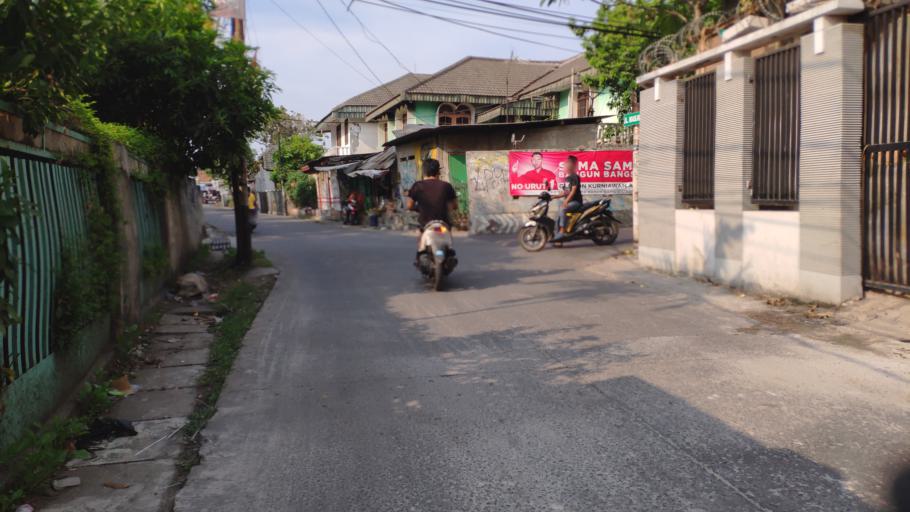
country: ID
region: West Java
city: Pamulang
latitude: -6.3198
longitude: 106.7938
